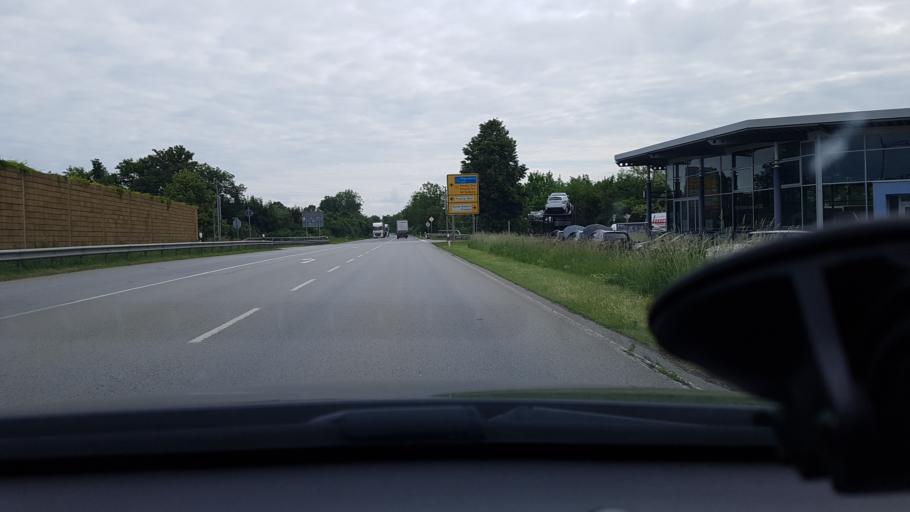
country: DE
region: Bavaria
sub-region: Lower Bavaria
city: Pocking
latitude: 48.3908
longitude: 13.3020
